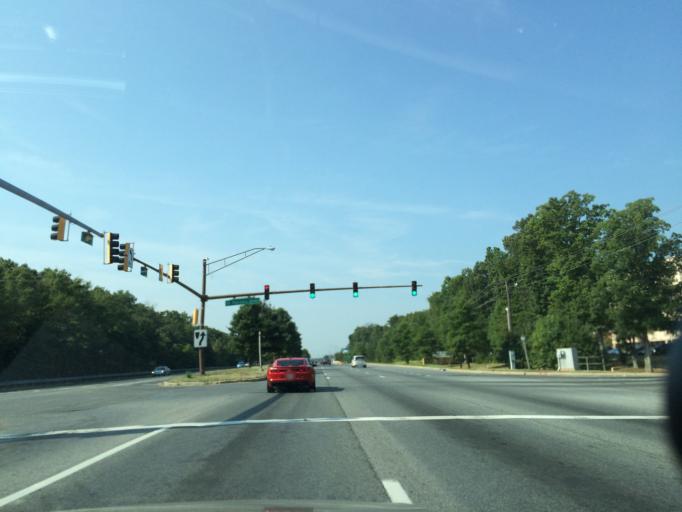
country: US
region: Maryland
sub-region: Charles County
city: Waldorf
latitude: 38.6186
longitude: -76.9187
